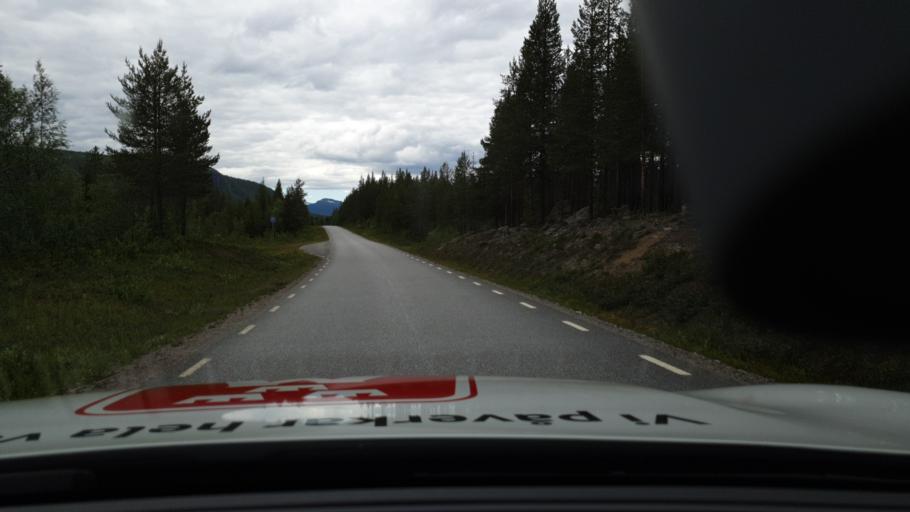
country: SE
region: Norrbotten
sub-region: Arjeplogs Kommun
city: Arjeplog
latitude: 66.8780
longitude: 18.1960
